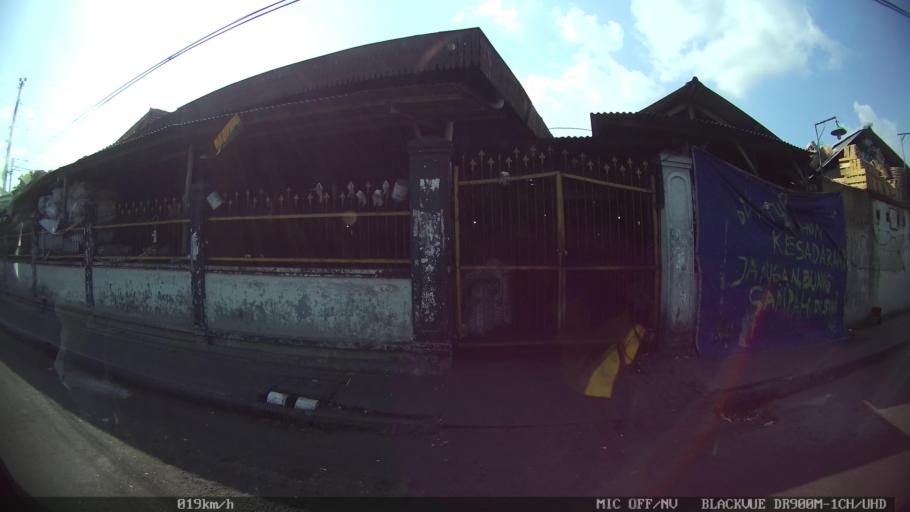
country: ID
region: Daerah Istimewa Yogyakarta
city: Yogyakarta
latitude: -7.8286
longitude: 110.3997
